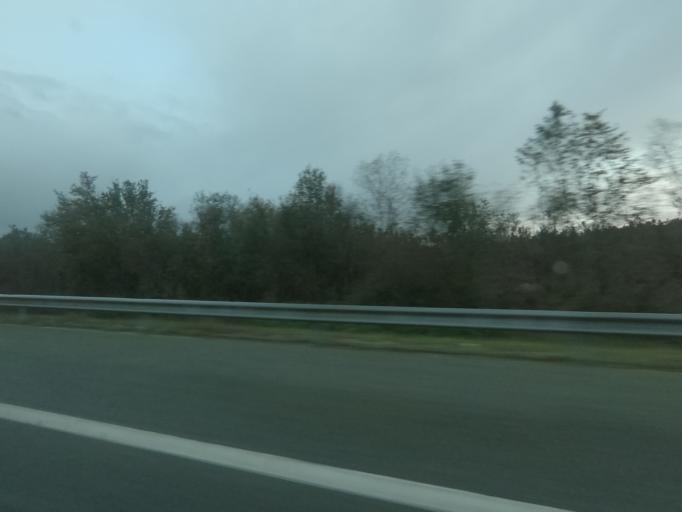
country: PT
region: Braga
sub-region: Vila Verde
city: Prado
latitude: 41.5472
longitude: -8.5046
